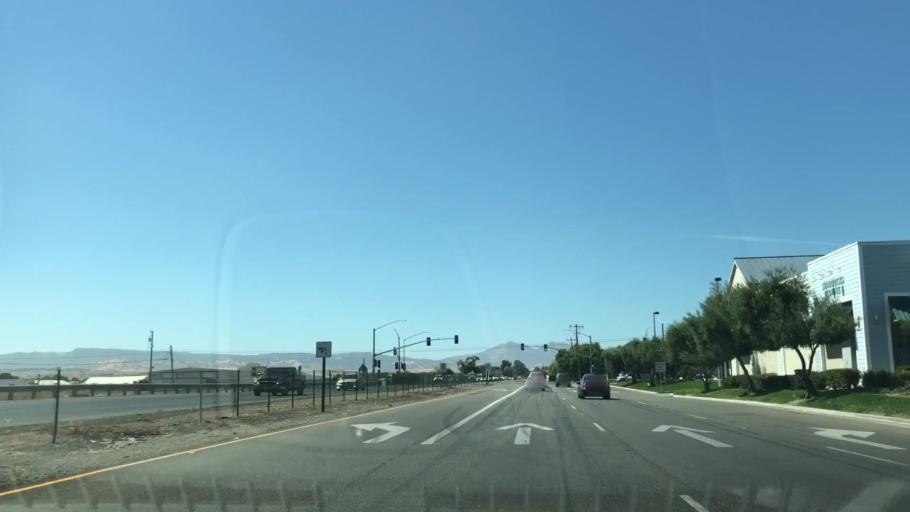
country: US
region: California
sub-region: Contra Costa County
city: Byron
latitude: 37.8894
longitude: -121.6214
